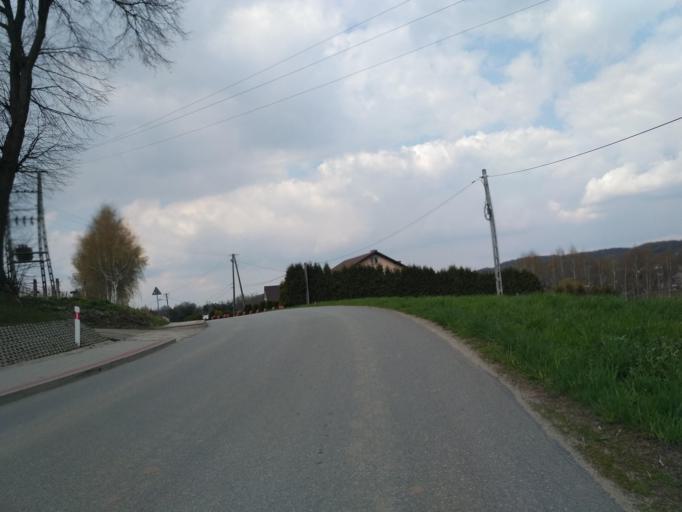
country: PL
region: Subcarpathian Voivodeship
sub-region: Powiat sanocki
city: Strachocina
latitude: 49.6040
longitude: 22.0921
